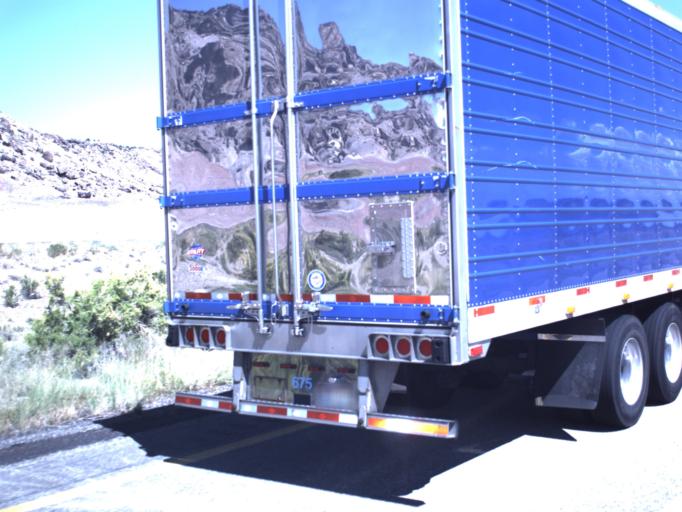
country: US
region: Utah
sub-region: Emery County
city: Ferron
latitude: 38.8186
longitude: -111.1576
